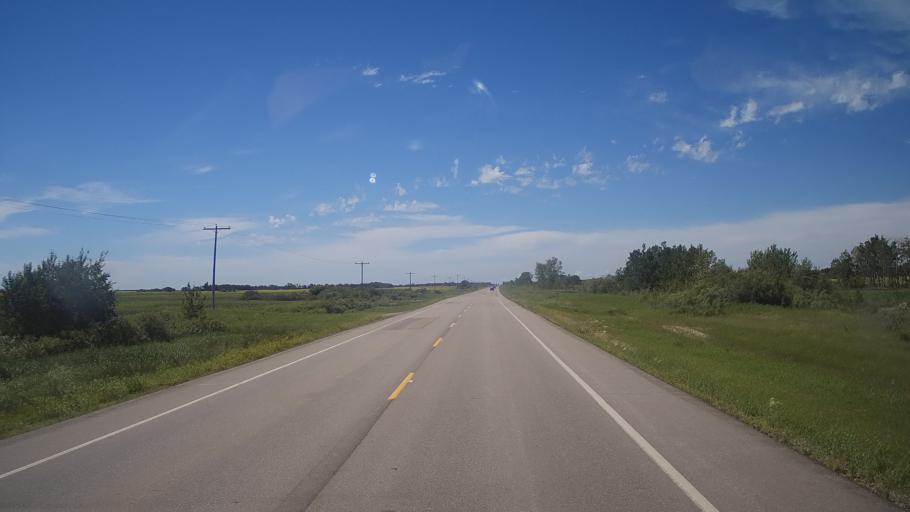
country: CA
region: Saskatchewan
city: Langenburg
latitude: 50.8028
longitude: -101.5843
